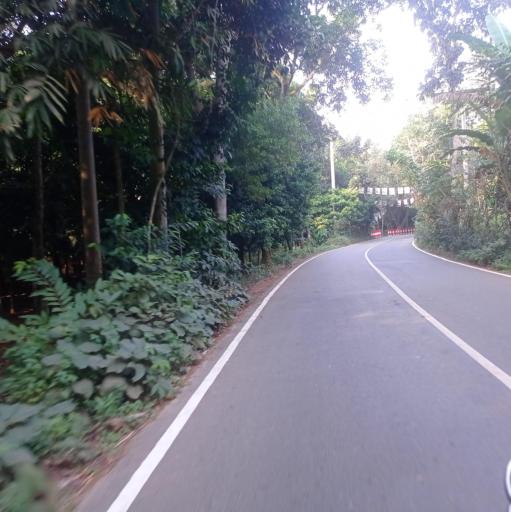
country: BD
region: Dhaka
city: Bhairab Bazar
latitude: 24.0532
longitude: 90.8347
